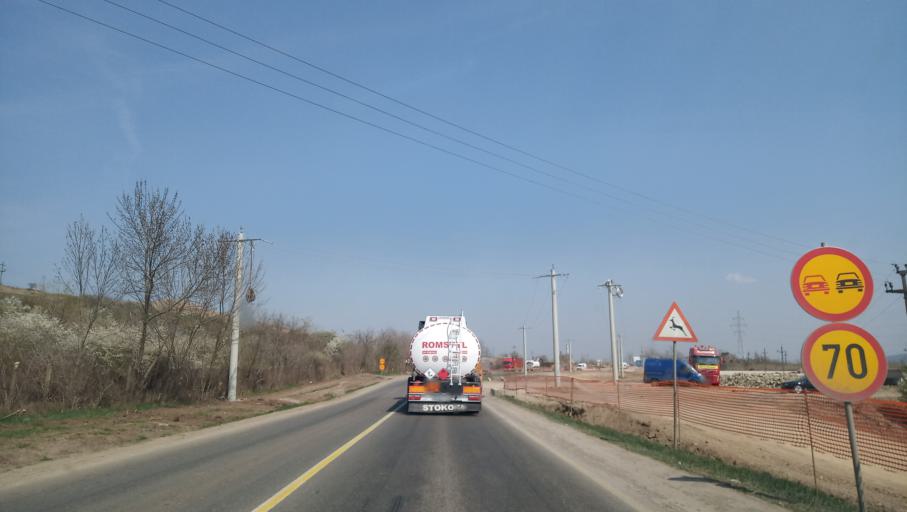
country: RO
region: Alba
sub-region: Municipiul Alba Iulia
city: Barabant
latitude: 46.1106
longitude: 23.6112
